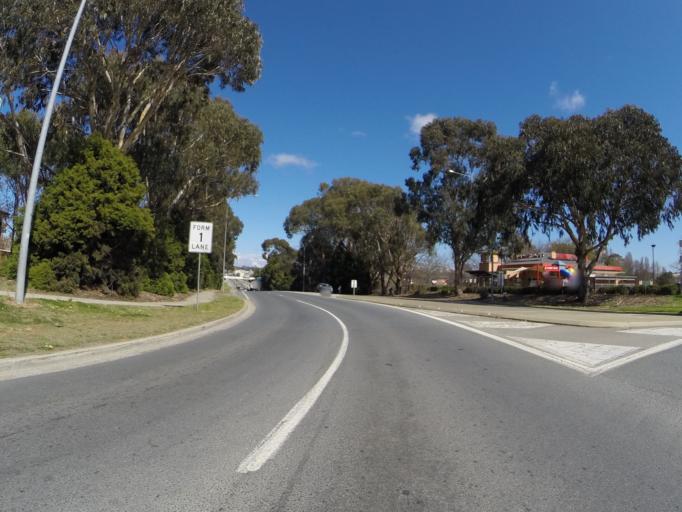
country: AU
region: New South Wales
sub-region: Queanbeyan
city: Queanbeyan
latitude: -35.3502
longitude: 149.2413
